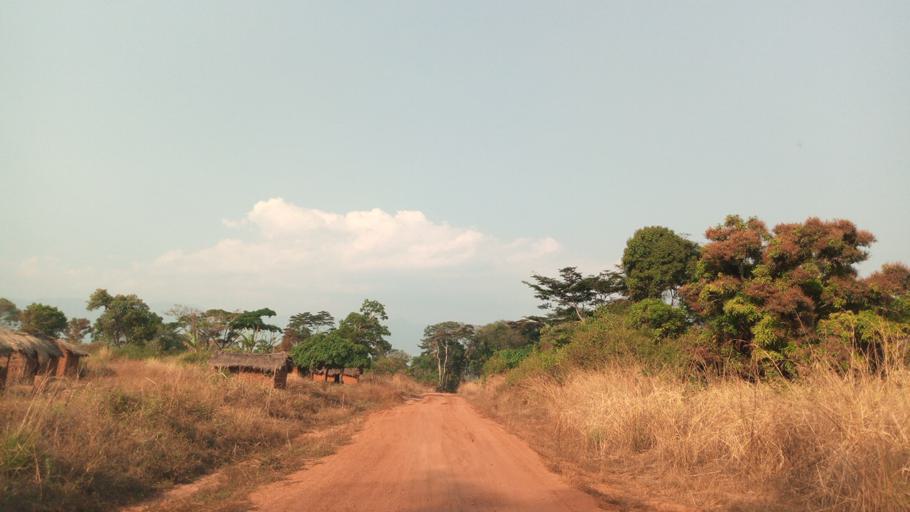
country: CD
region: Katanga
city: Kalemie
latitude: -5.2020
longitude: 28.8730
